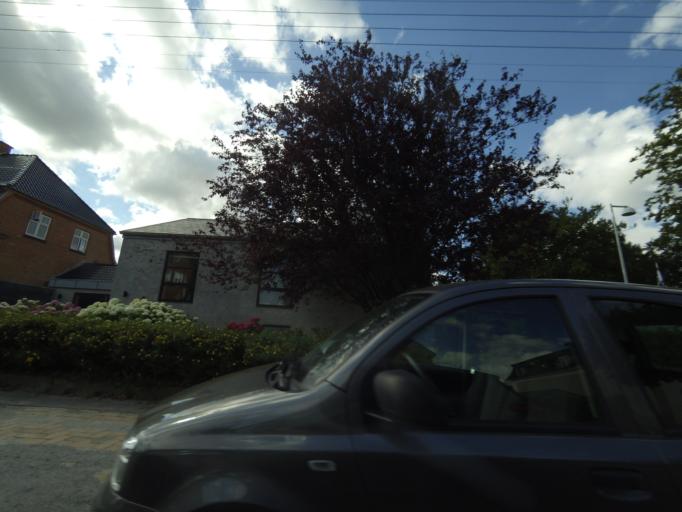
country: DK
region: South Denmark
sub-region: Odense Kommune
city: Odense
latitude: 55.3849
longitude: 10.3929
